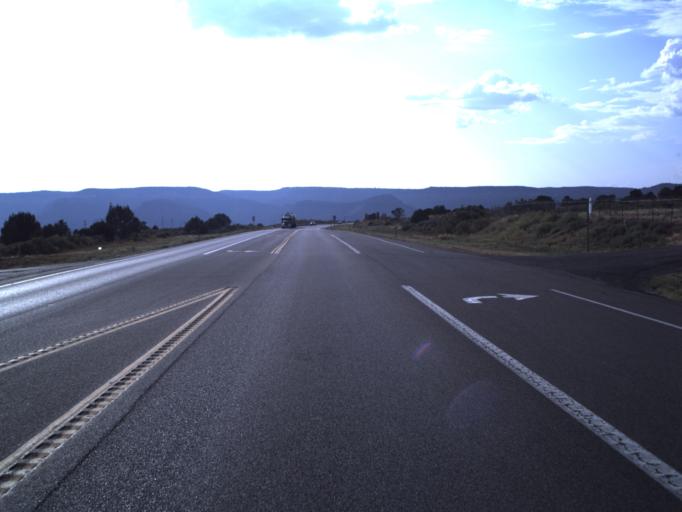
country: US
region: Utah
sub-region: Kane County
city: Kanab
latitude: 37.0287
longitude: -112.4830
